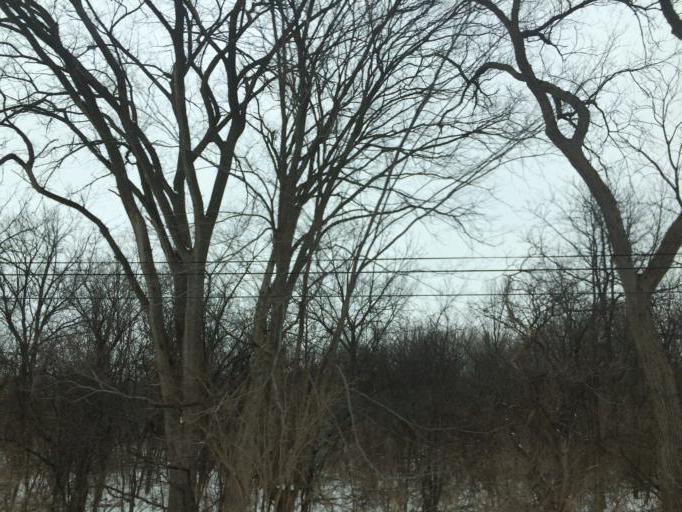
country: US
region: Illinois
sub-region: McHenry County
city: Harvard
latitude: 42.3923
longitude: -88.6020
